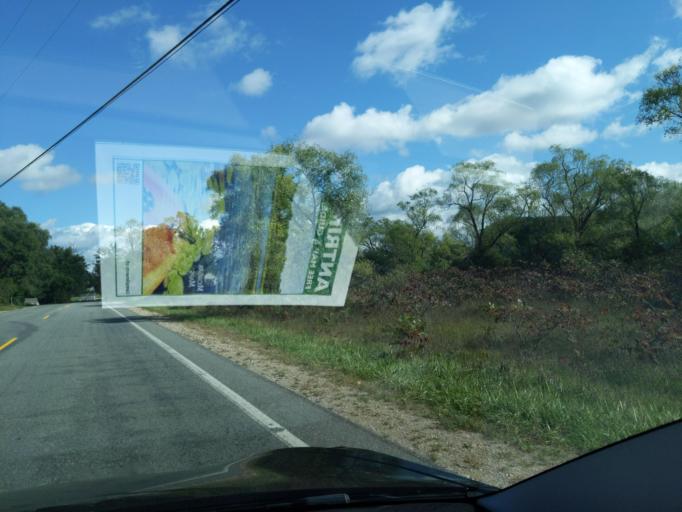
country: US
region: Michigan
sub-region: Antrim County
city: Elk Rapids
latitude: 44.9332
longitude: -85.3633
